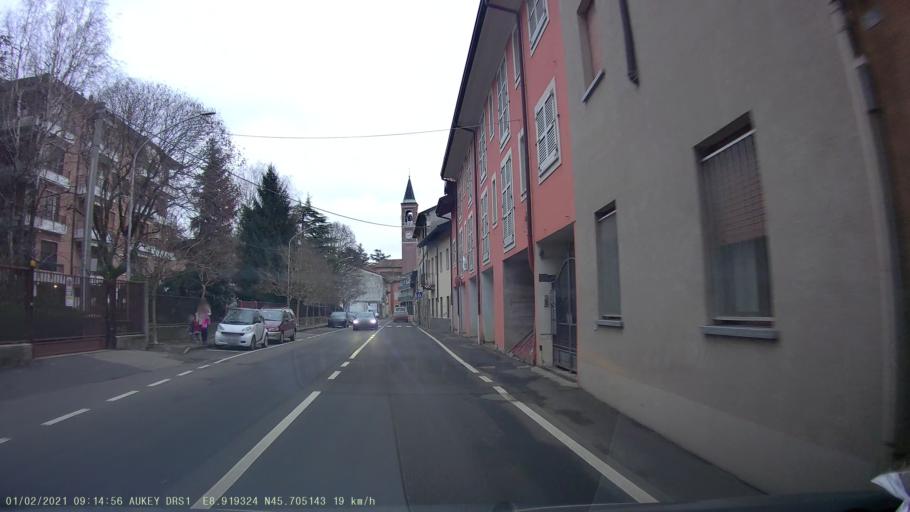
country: IT
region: Lombardy
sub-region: Provincia di Varese
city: Tradate
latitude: 45.7051
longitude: 8.9194
